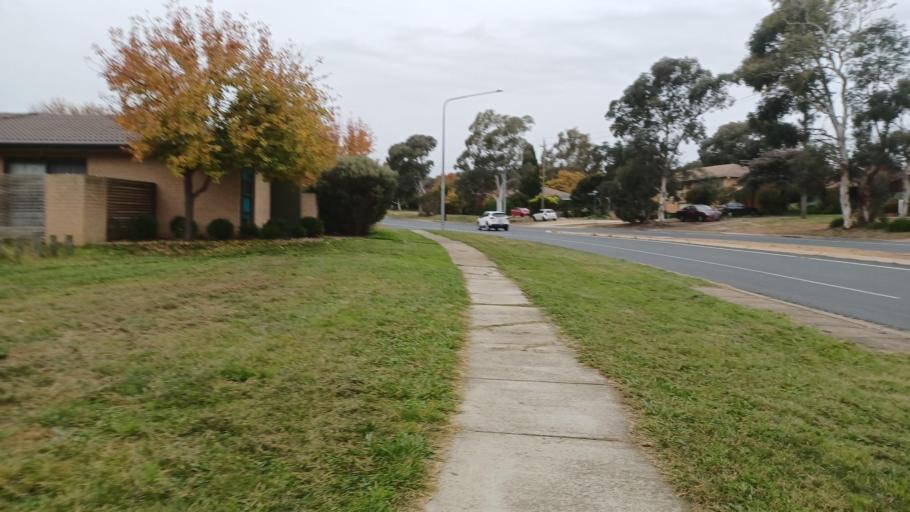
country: AU
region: Australian Capital Territory
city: Belconnen
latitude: -35.2044
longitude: 149.0387
